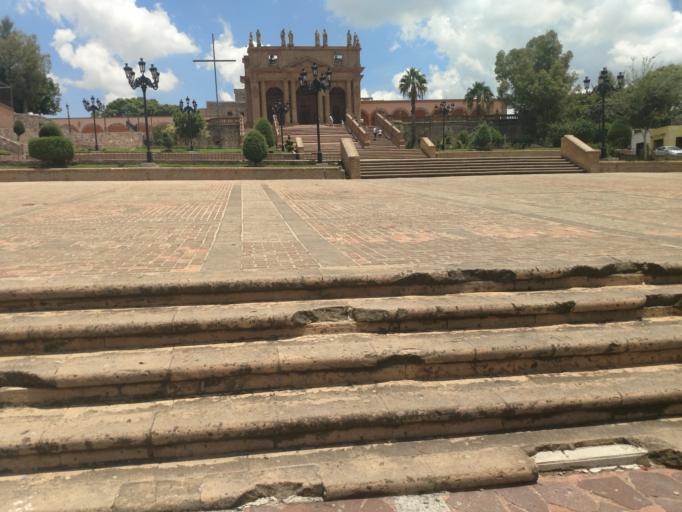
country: MX
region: Jalisco
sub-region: Lagos de Moreno
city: Lagos de Moreno
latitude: 21.3609
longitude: -101.9344
